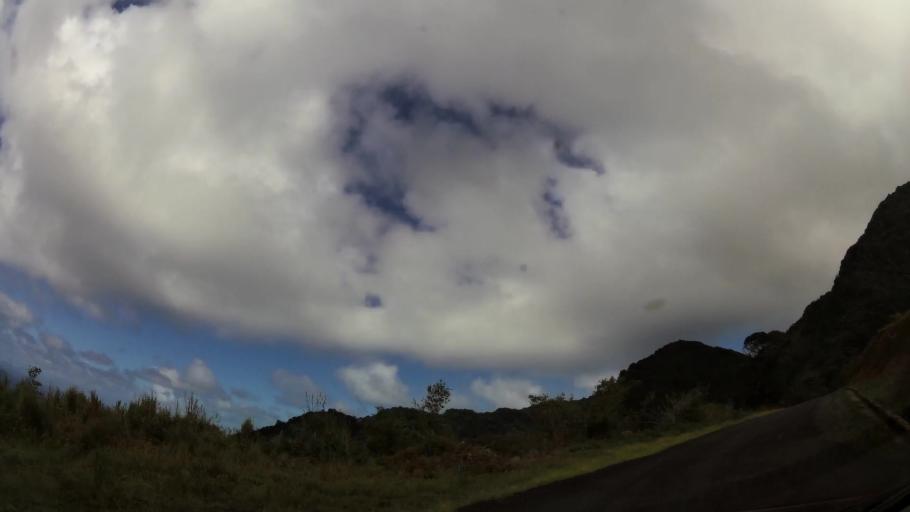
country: DM
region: Saint John
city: Portsmouth
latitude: 15.6139
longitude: -61.4481
